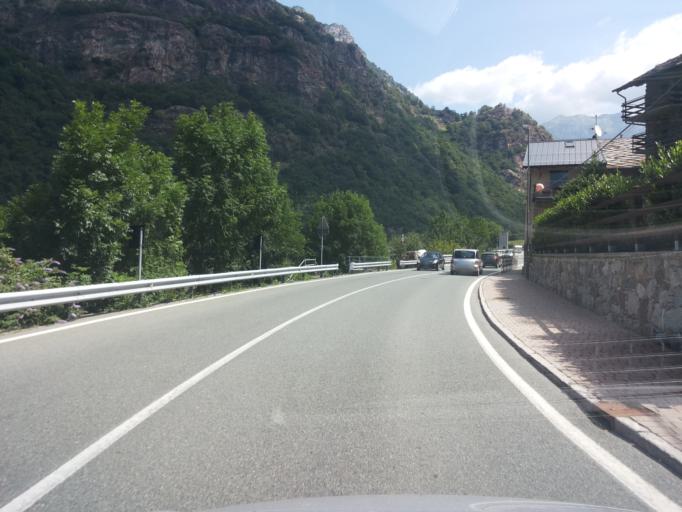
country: IT
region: Aosta Valley
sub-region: Valle d'Aosta
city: Perloz
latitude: 45.6198
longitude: 7.8196
